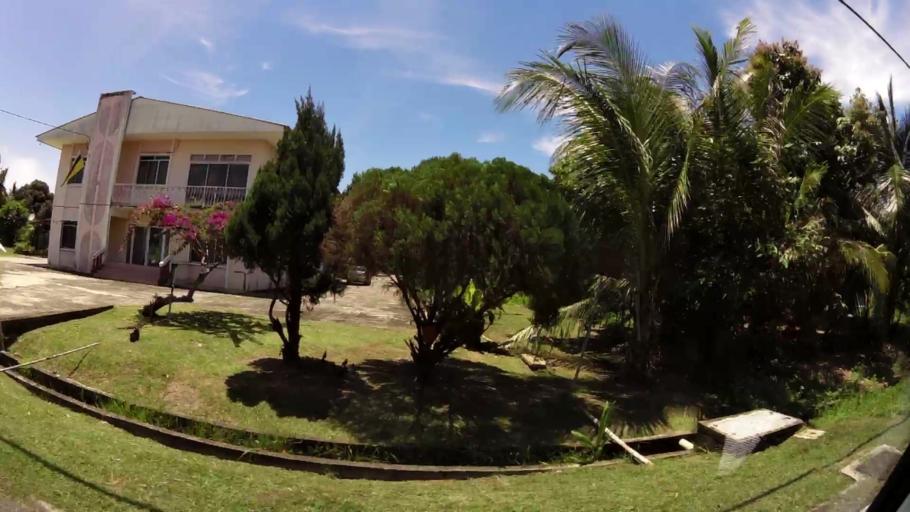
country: BN
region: Brunei and Muara
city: Bandar Seri Begawan
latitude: 4.9317
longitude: 114.9336
